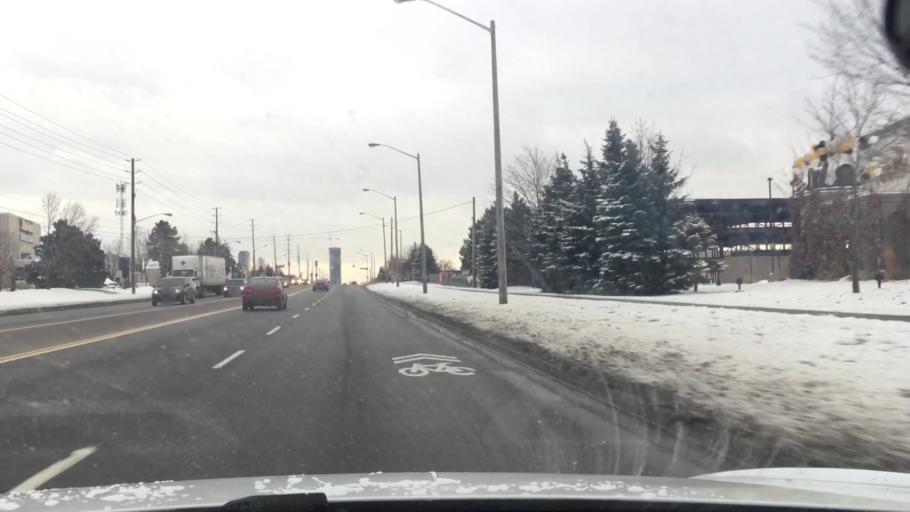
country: CA
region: Ontario
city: Vaughan
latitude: 43.8175
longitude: -79.5296
